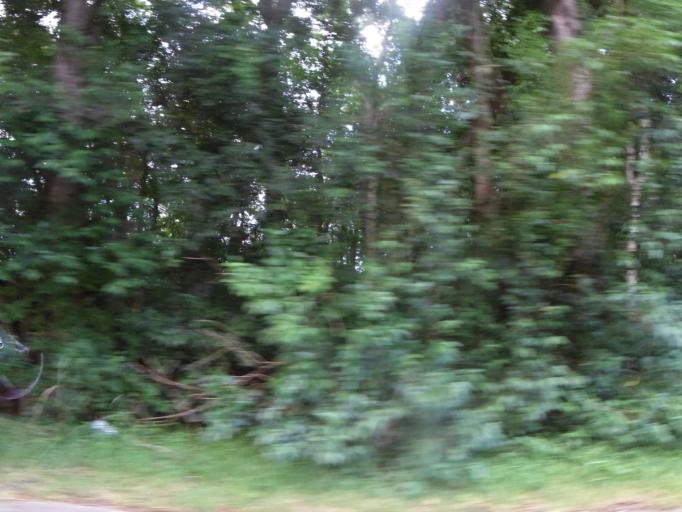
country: US
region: Florida
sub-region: Duval County
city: Jacksonville
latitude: 30.3634
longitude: -81.7091
